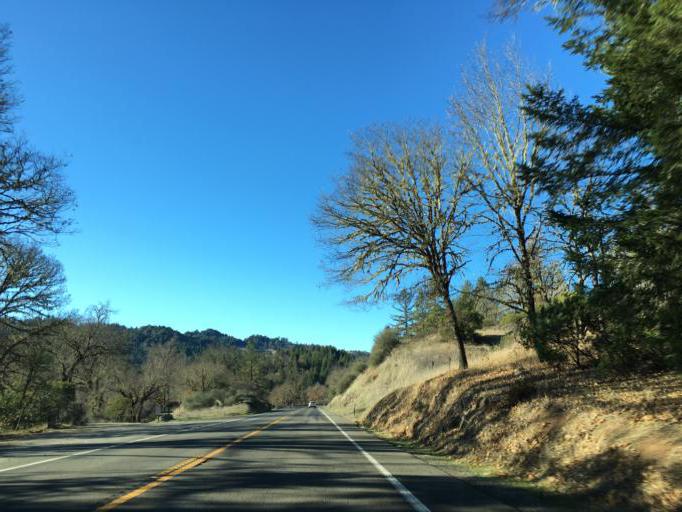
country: US
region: California
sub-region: Mendocino County
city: Laytonville
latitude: 39.7487
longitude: -123.5300
